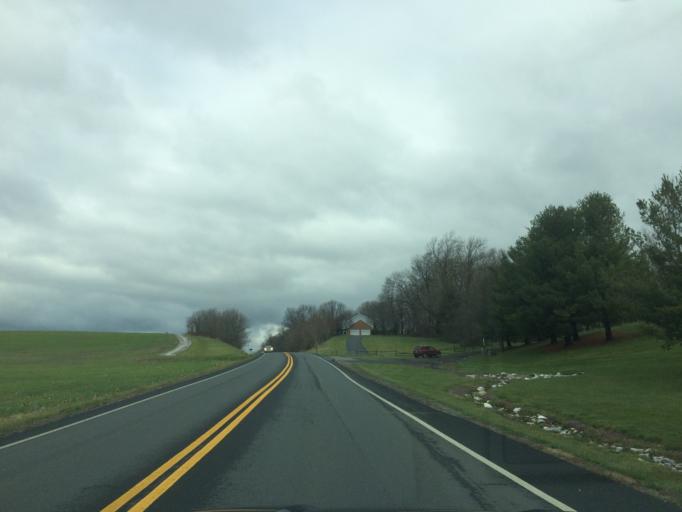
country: US
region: Maryland
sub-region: Carroll County
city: Westminster
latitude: 39.5415
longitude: -77.0070
